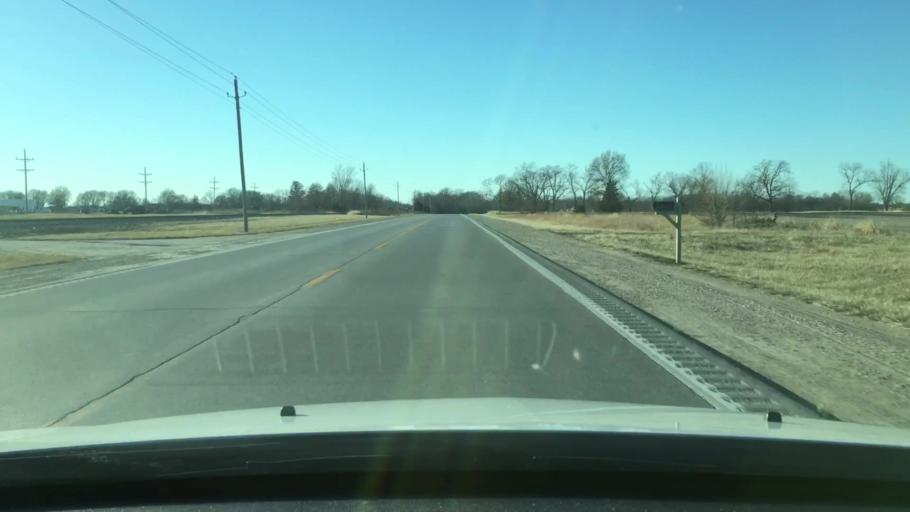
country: US
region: Missouri
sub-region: Audrain County
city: Mexico
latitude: 39.1885
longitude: -91.9725
